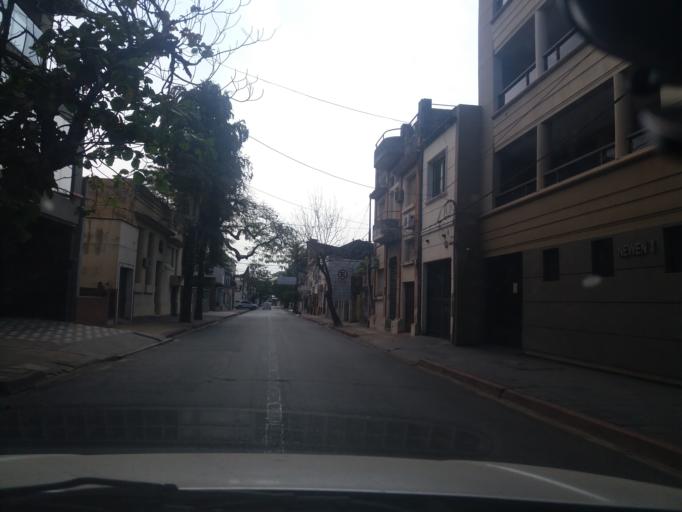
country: AR
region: Corrientes
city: Corrientes
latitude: -27.4717
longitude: -58.8385
